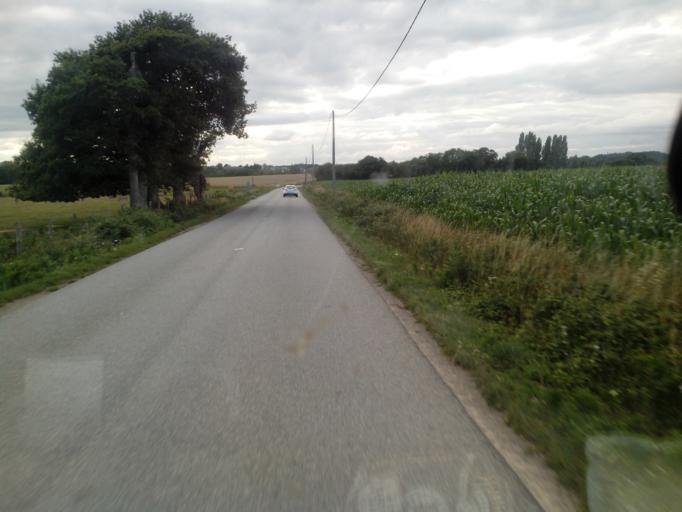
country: FR
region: Brittany
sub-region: Departement du Morbihan
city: Mauron
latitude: 48.0772
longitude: -2.2595
